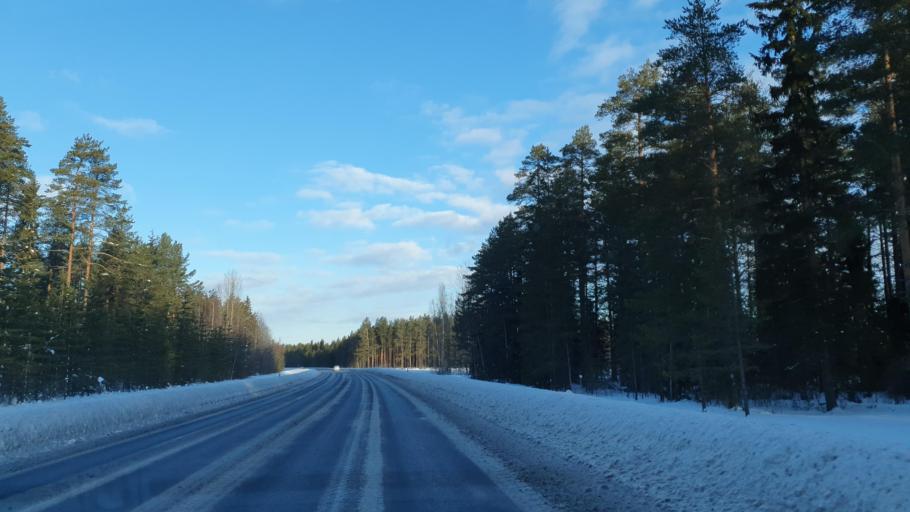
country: FI
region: Northern Ostrobothnia
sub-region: Oulunkaari
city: Utajaervi
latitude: 64.6954
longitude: 26.5368
